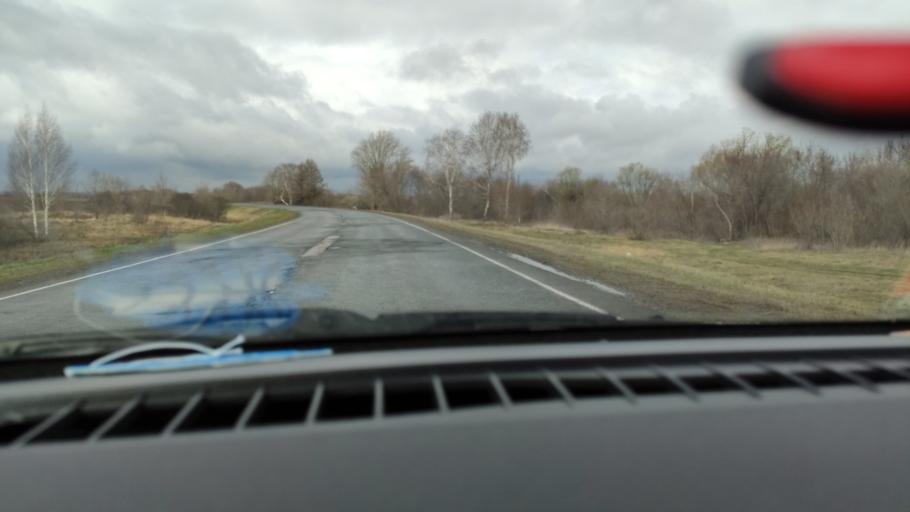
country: RU
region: Samara
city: Koshki
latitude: 54.1862
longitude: 50.5037
